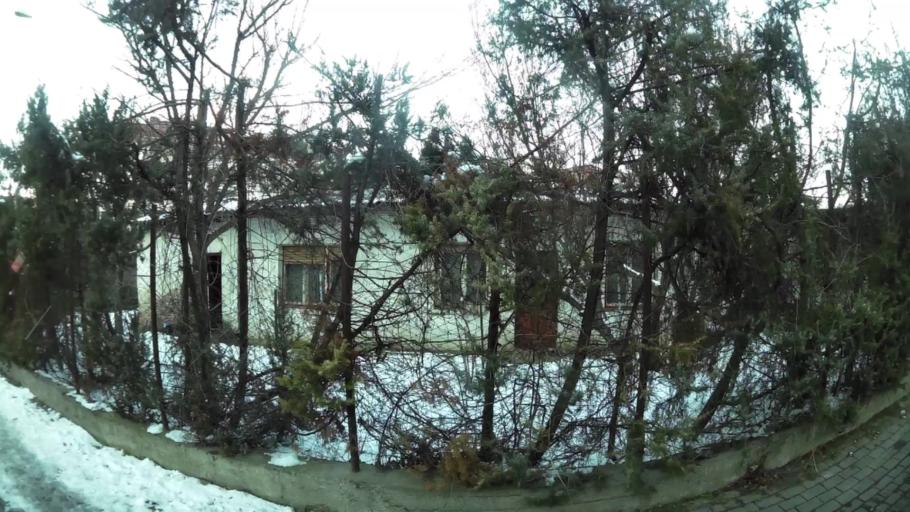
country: MK
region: Karpos
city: Skopje
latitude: 41.9933
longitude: 21.4098
